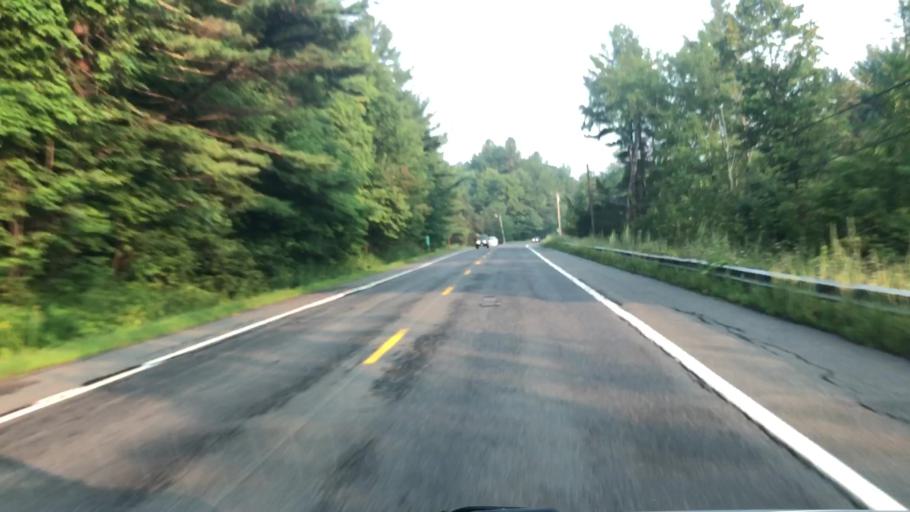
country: US
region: Massachusetts
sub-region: Franklin County
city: Shelburne
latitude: 42.6100
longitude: -72.6580
